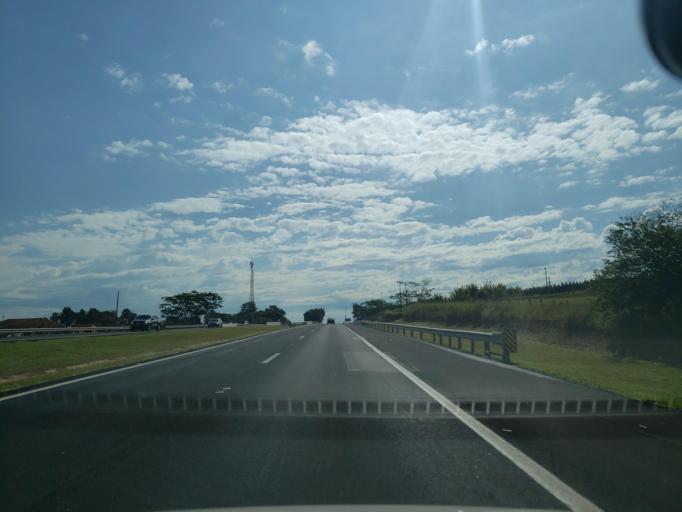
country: BR
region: Sao Paulo
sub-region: Pirajui
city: Pirajui
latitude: -22.0010
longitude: -49.4303
